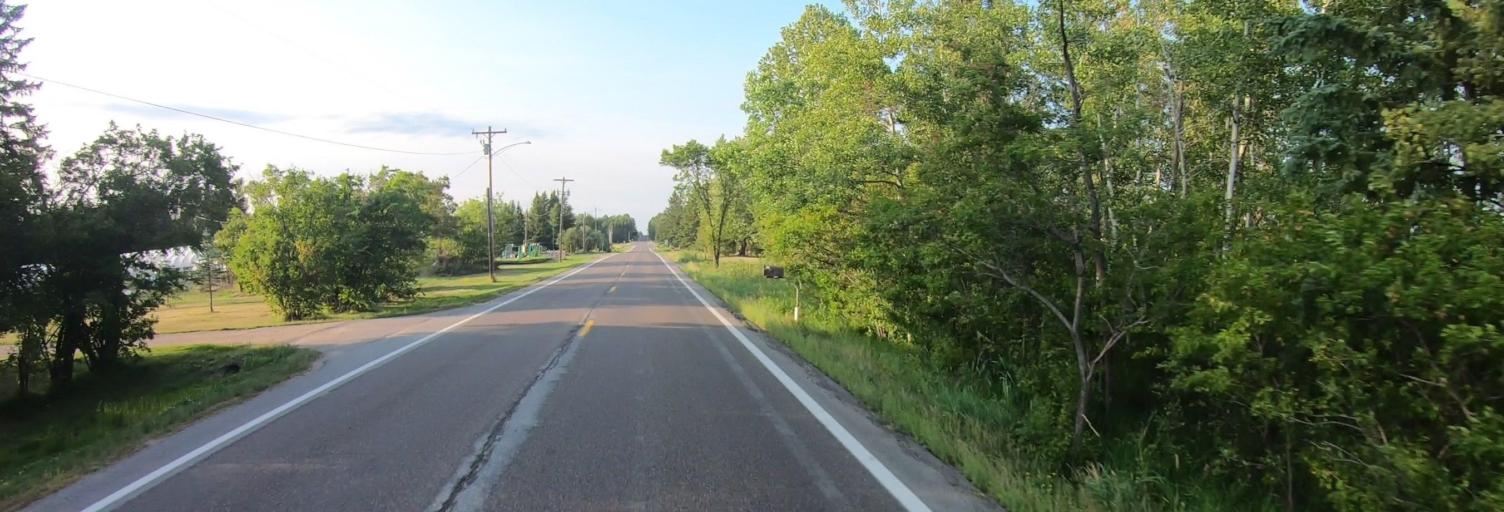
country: US
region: Minnesota
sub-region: Saint Louis County
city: Mountain Iron
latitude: 47.8575
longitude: -92.6843
